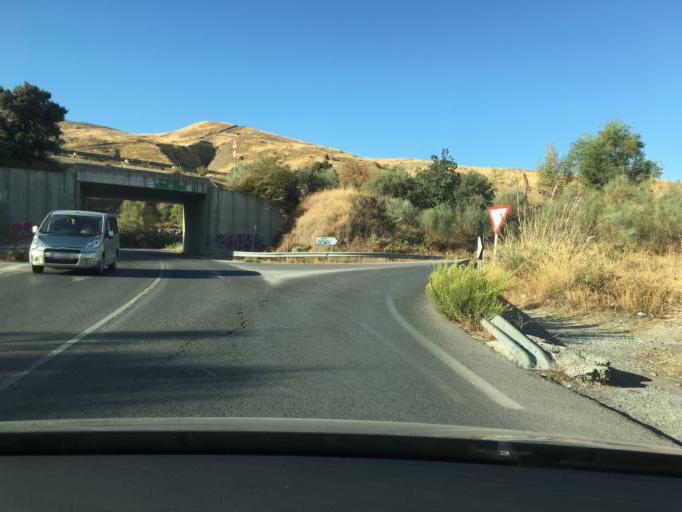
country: ES
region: Andalusia
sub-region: Provincia de Granada
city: Cenes de la Vega
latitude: 37.1544
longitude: -3.5334
